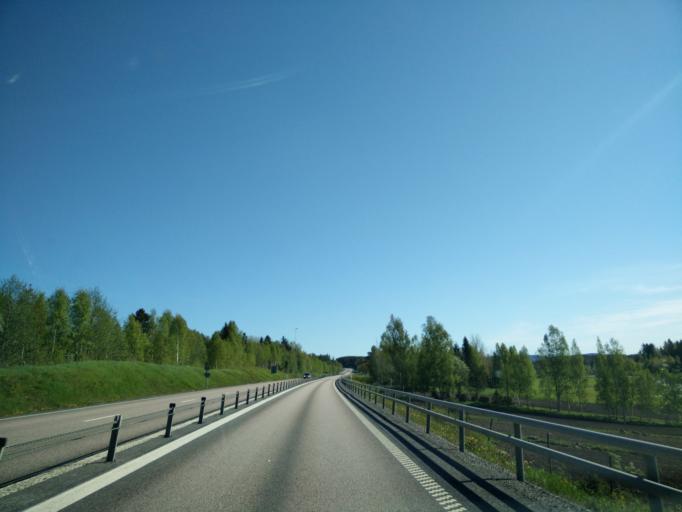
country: SE
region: Vaesternorrland
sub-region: Haernoesands Kommun
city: Haernoesand
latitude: 62.8549
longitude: 18.0147
